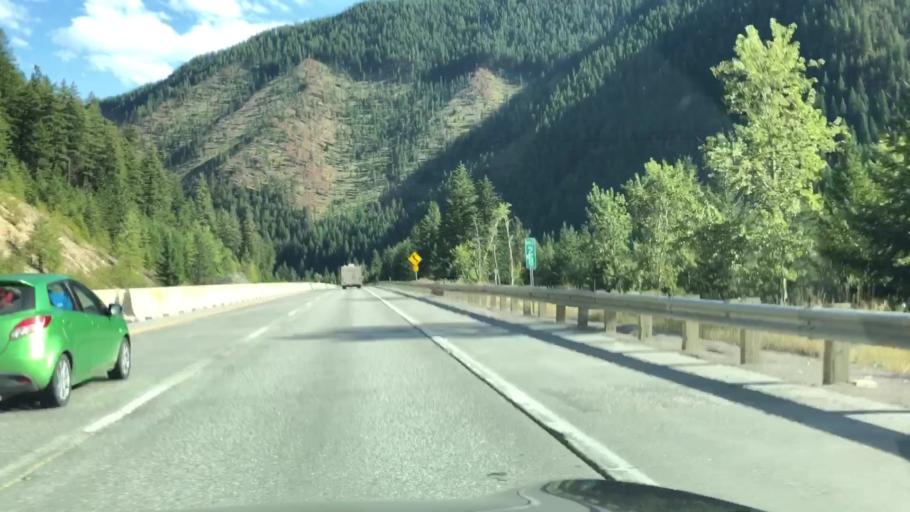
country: US
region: Montana
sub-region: Sanders County
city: Thompson Falls
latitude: 47.3055
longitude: -115.2045
